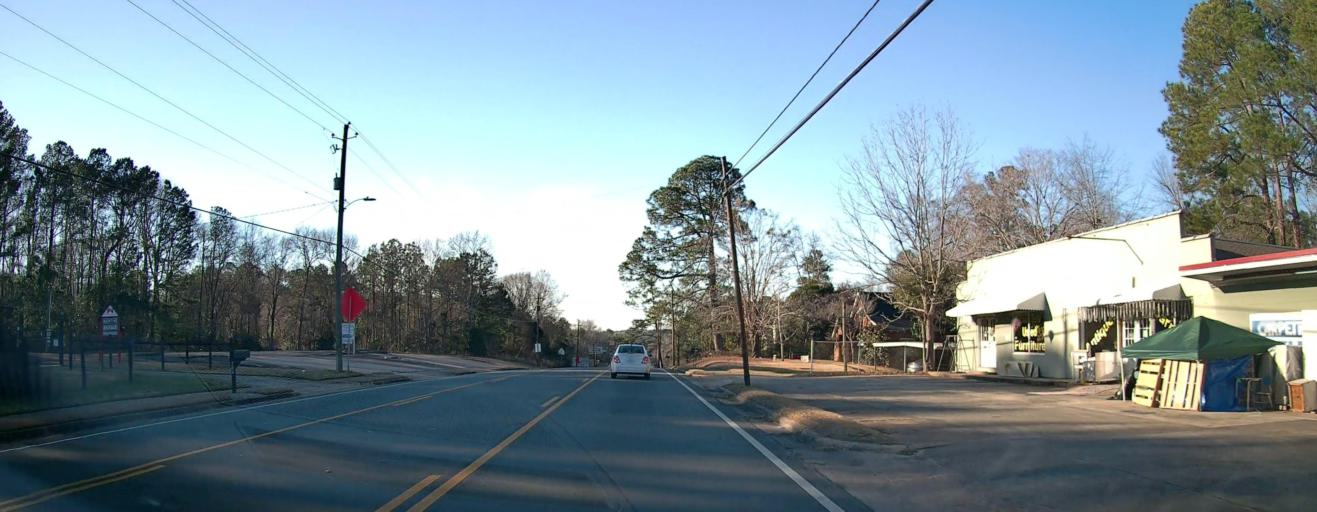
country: US
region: Georgia
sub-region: Meriwether County
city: Manchester
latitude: 32.8615
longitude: -84.6231
